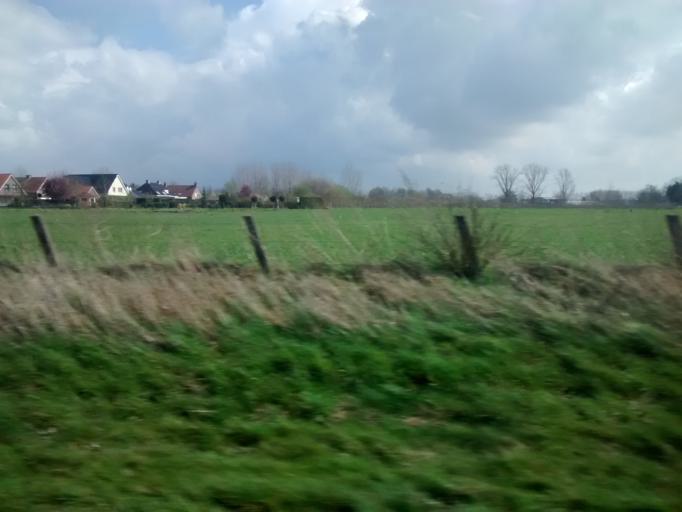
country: NL
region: Limburg
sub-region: Gemeente Maasgouw
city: Maasbracht
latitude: 51.0944
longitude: 5.8763
